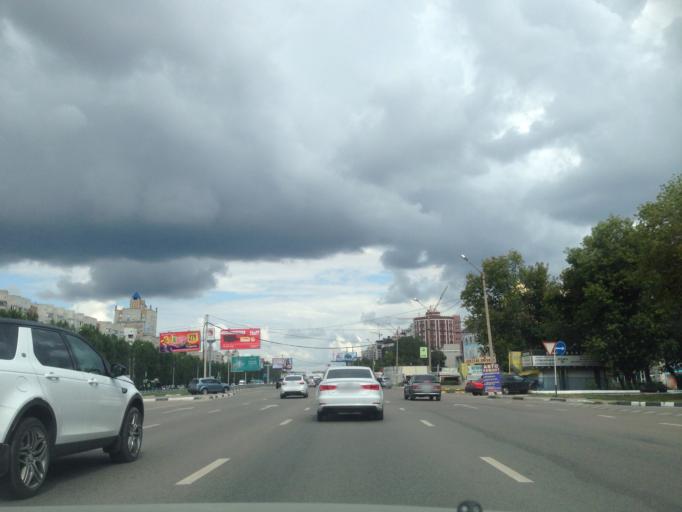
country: RU
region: Voronezj
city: Voronezh
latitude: 51.7082
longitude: 39.1813
